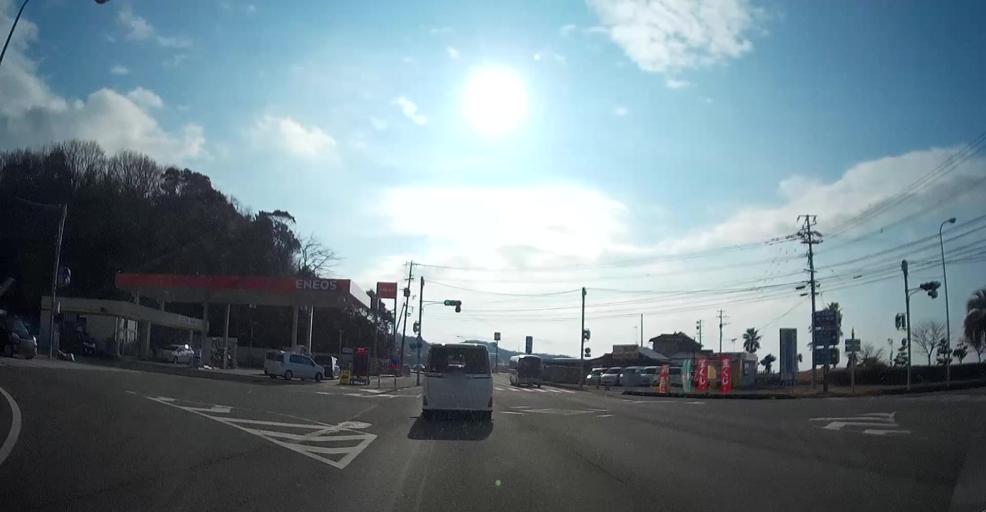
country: JP
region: Kumamoto
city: Yatsushiro
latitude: 32.5760
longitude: 130.4204
